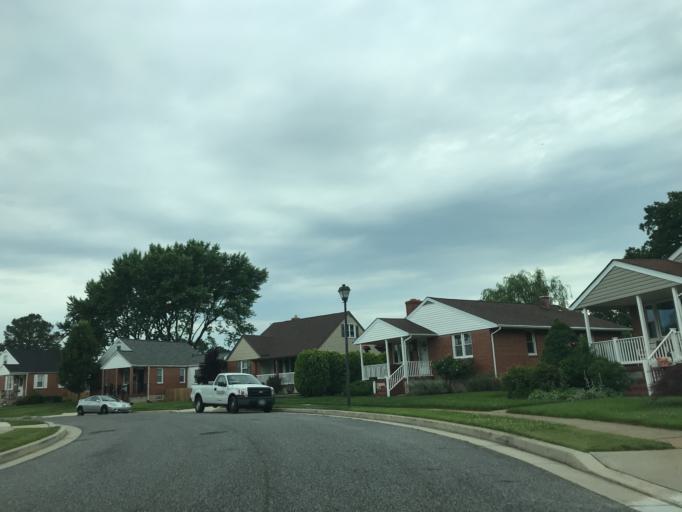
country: US
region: Maryland
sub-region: Baltimore County
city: Overlea
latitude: 39.3627
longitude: -76.5169
